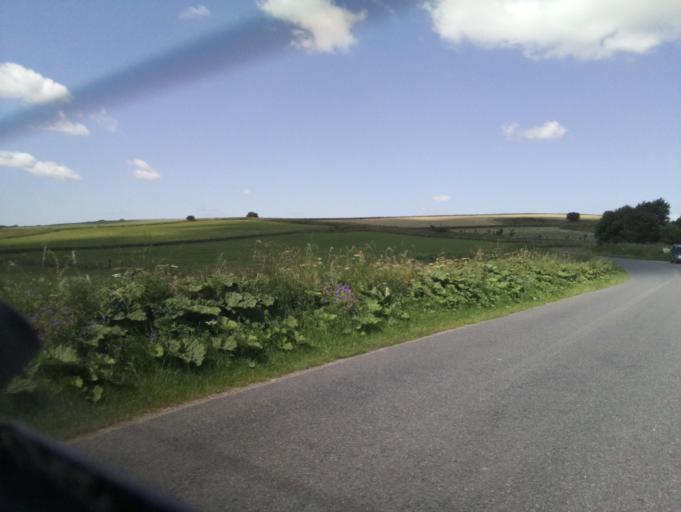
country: GB
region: England
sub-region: Derbyshire
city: Tideswell
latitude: 53.2292
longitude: -1.7855
